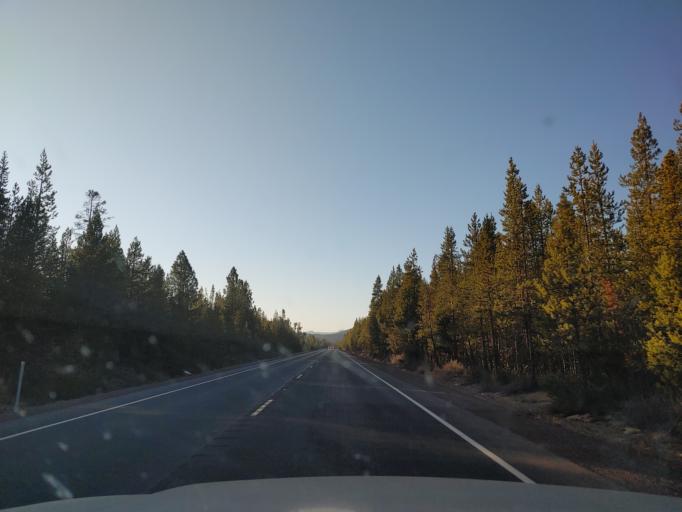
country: US
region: Oregon
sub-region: Deschutes County
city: La Pine
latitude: 43.3977
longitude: -121.8183
